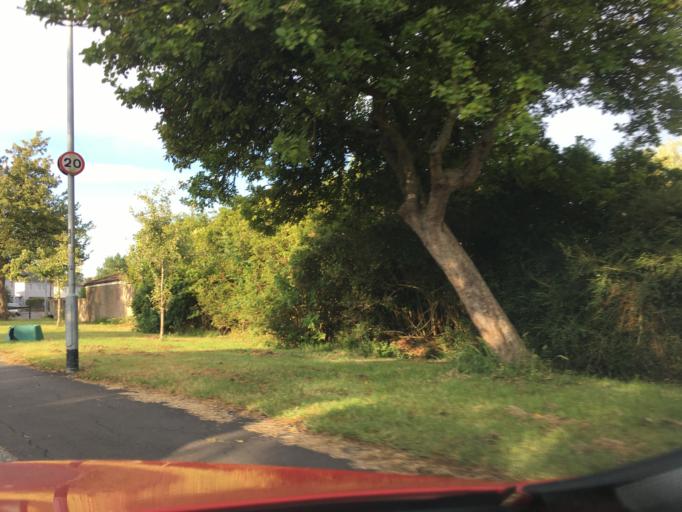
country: GB
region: England
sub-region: Bristol
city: Bristol
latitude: 51.4926
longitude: -2.5868
